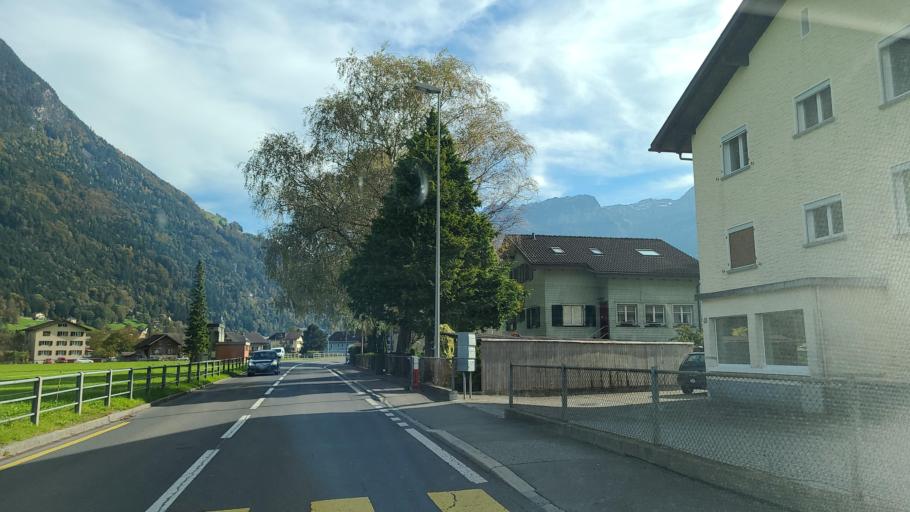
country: CH
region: Uri
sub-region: Uri
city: Seedorf
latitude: 46.8841
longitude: 8.6246
